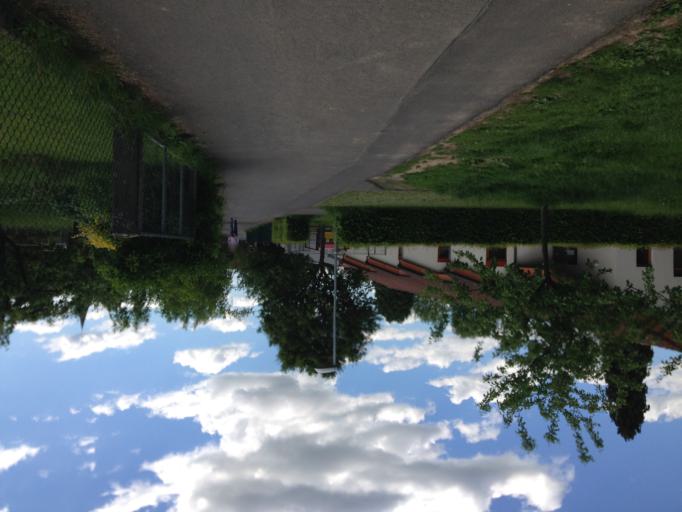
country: DE
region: Hesse
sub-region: Regierungsbezirk Giessen
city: Heuchelheim
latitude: 50.5849
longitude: 8.6286
